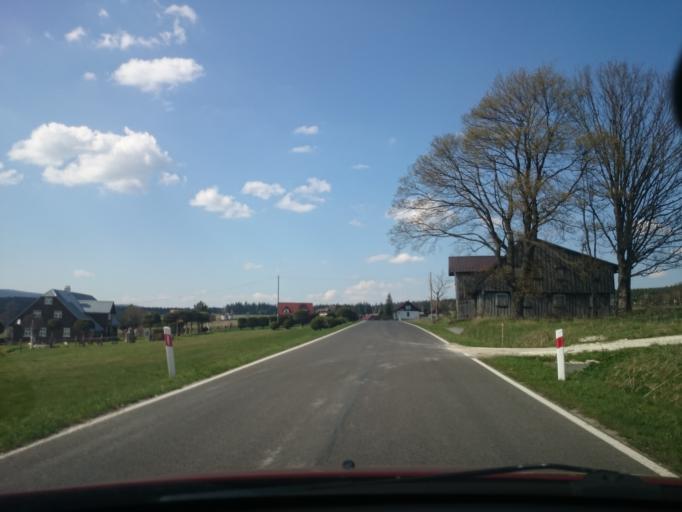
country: PL
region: Lower Silesian Voivodeship
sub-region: Powiat klodzki
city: Szczytna
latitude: 50.3088
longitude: 16.4503
